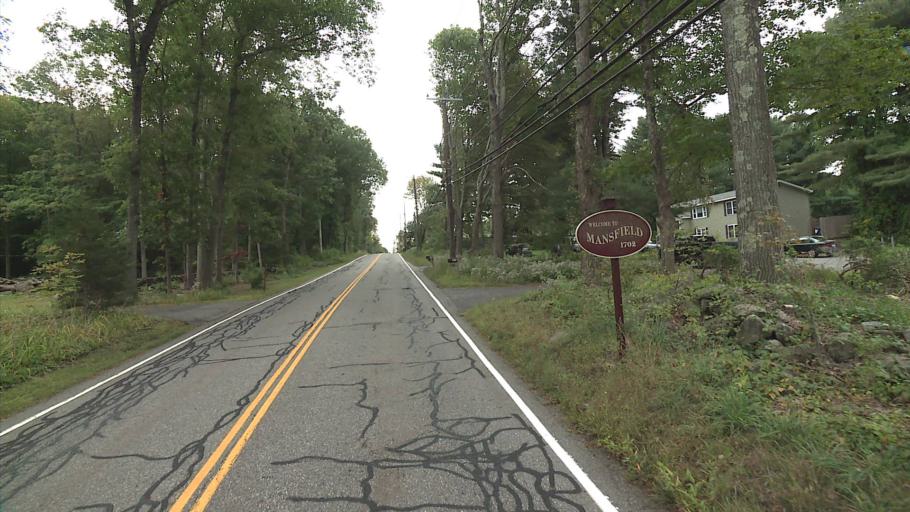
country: US
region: Connecticut
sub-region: Tolland County
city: Storrs
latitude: 41.8356
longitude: -72.2696
